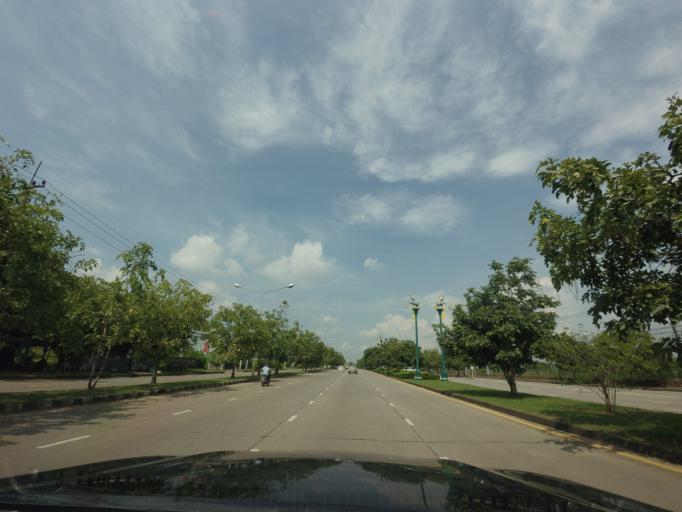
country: TH
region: Khon Kaen
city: Khon Kaen
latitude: 16.4420
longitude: 102.8120
